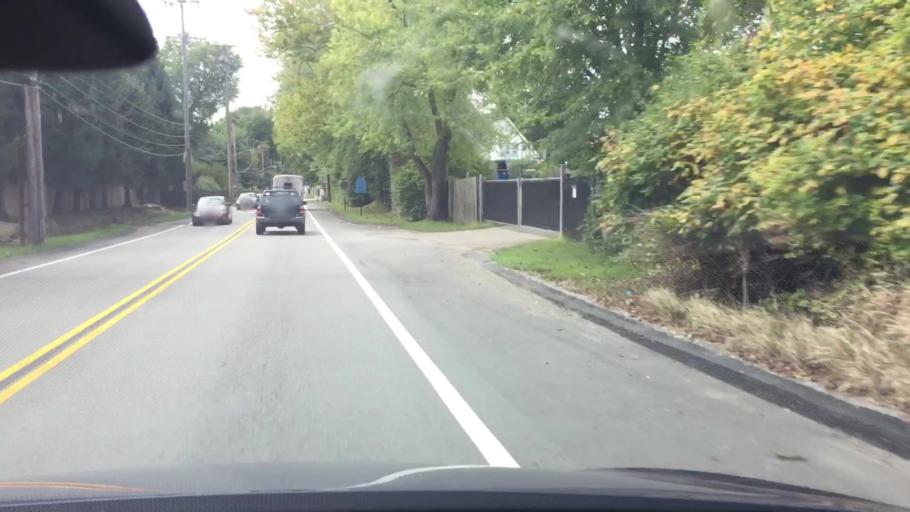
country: US
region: Pennsylvania
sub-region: Allegheny County
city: Oakmont
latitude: 40.5252
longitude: -79.8255
